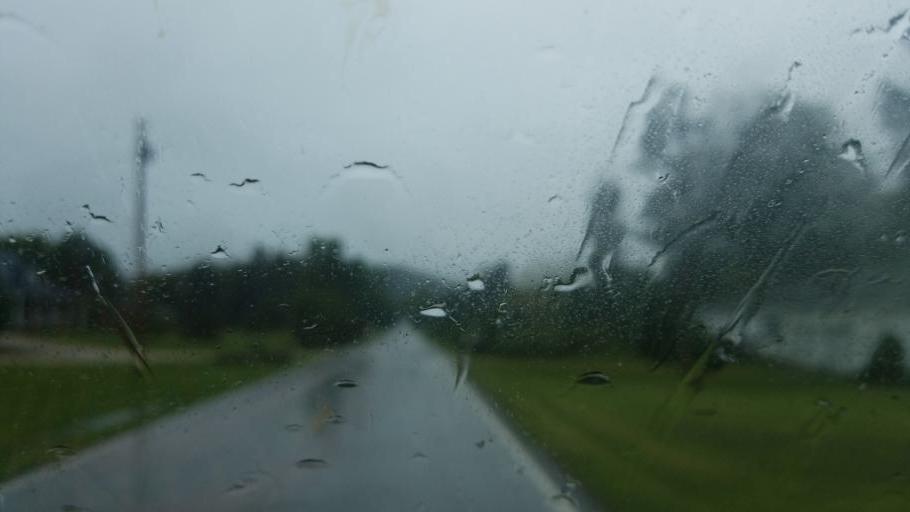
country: US
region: Kentucky
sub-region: Greenup County
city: South Shore
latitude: 38.6869
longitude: -82.9234
